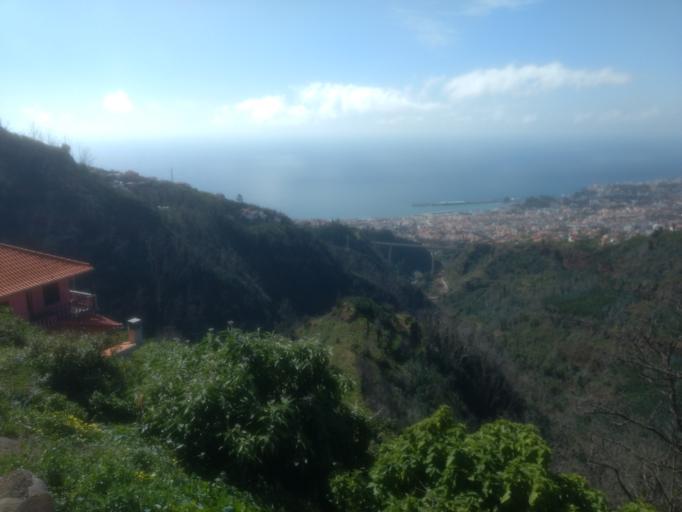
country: PT
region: Madeira
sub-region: Funchal
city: Nossa Senhora do Monte
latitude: 32.6750
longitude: -16.8927
